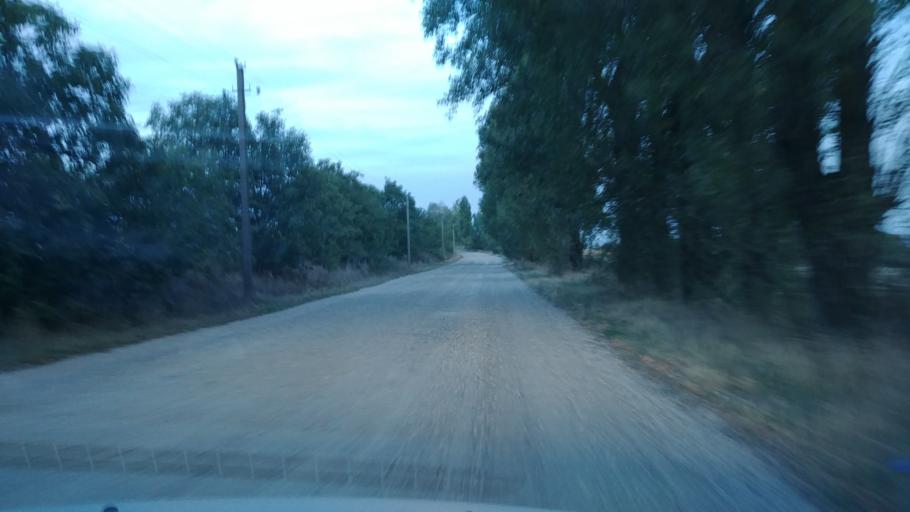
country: MD
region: Rezina
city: Saharna
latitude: 47.6775
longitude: 28.9248
